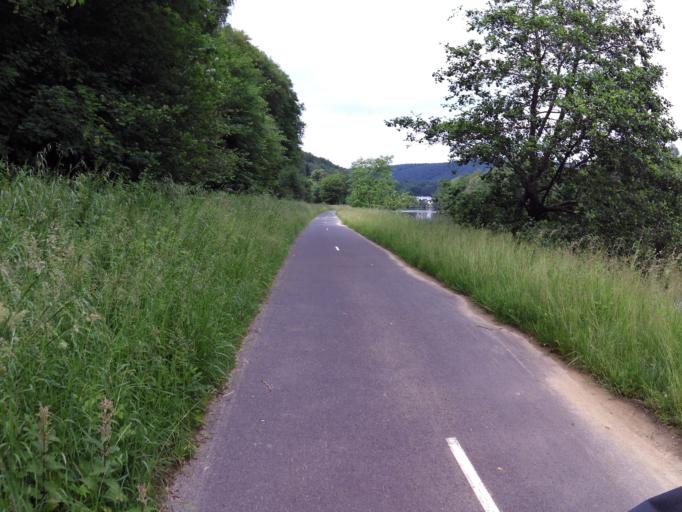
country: FR
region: Champagne-Ardenne
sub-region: Departement des Ardennes
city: Nouzonville
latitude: 49.8052
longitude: 4.7468
